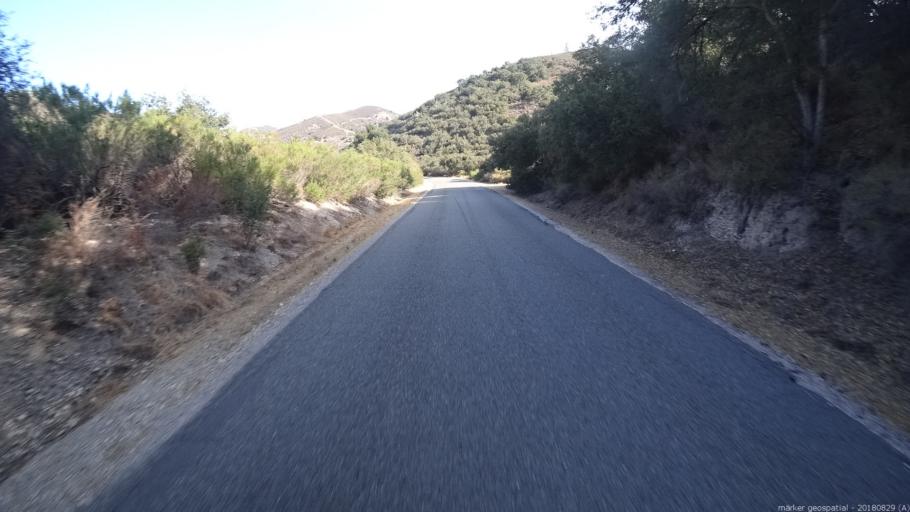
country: US
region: California
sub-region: Monterey County
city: King City
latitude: 36.0343
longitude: -121.0768
